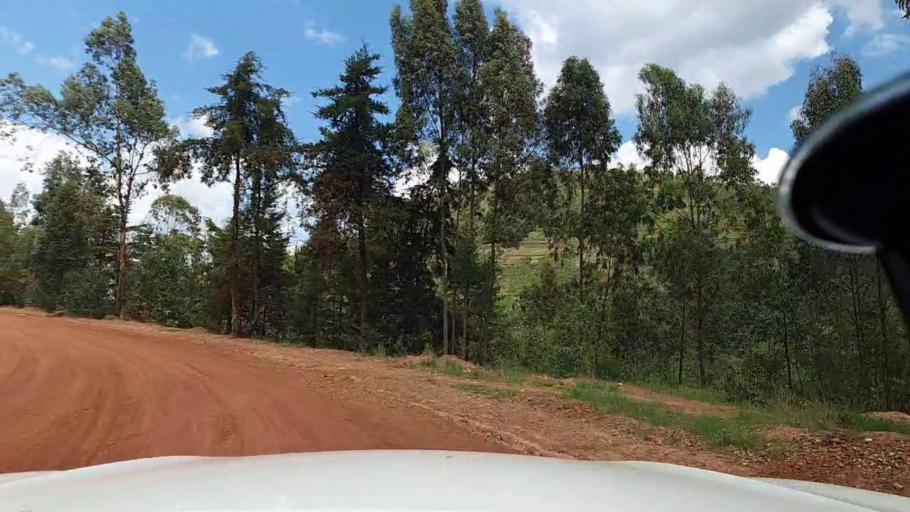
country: RW
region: Northern Province
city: Byumba
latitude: -1.7562
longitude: 29.8501
